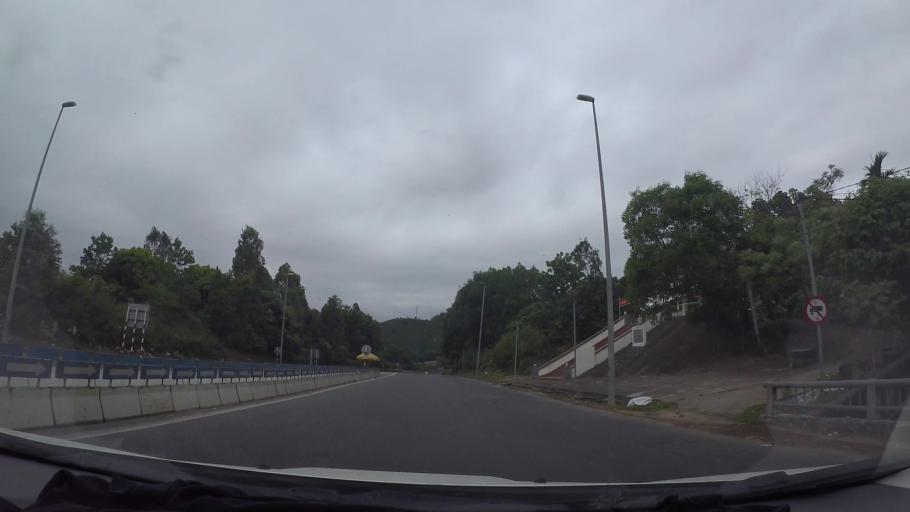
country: VN
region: Da Nang
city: Lien Chieu
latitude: 16.1309
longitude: 108.1041
